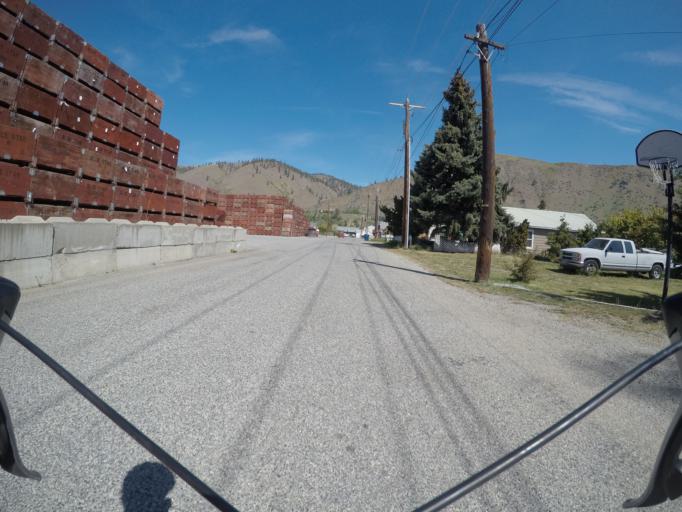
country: US
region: Washington
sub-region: Chelan County
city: Cashmere
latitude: 47.5185
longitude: -120.4602
